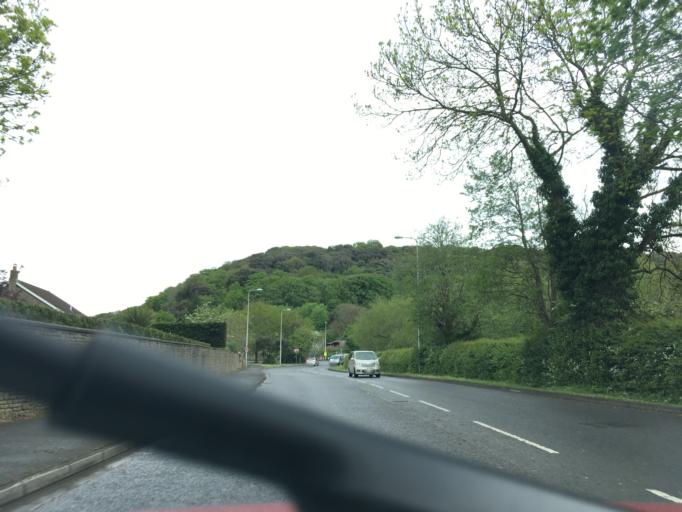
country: GB
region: England
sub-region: North Somerset
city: Clevedon
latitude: 51.4381
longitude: -2.8387
